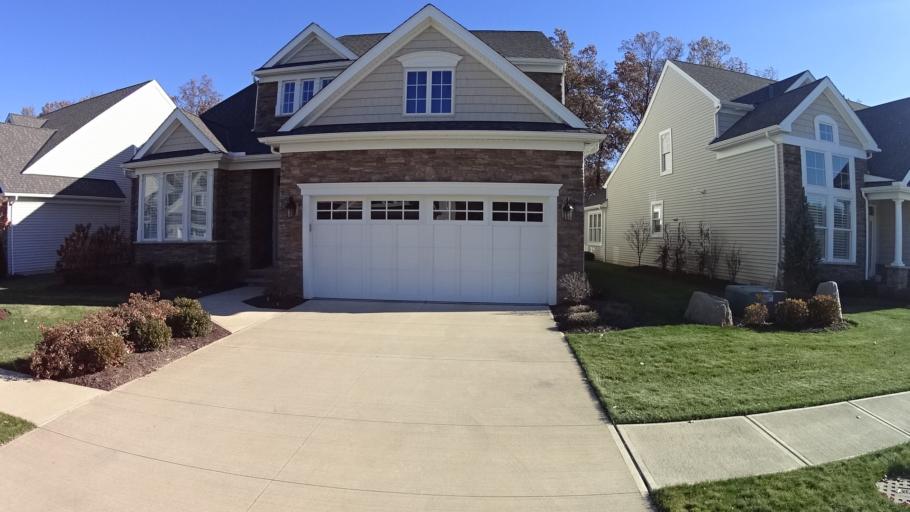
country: US
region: Ohio
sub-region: Lorain County
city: Avon Center
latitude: 41.4812
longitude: -82.0089
